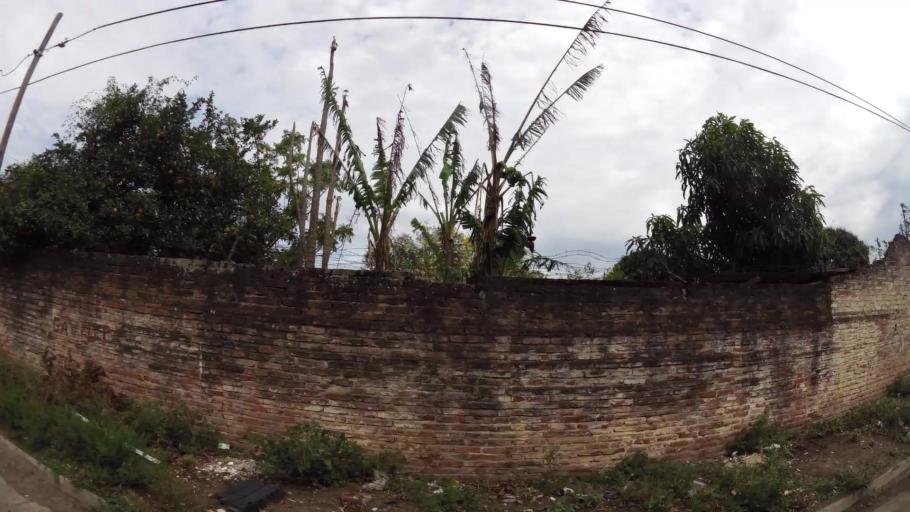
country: BO
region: Santa Cruz
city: Santa Cruz de la Sierra
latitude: -17.7493
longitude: -63.1929
